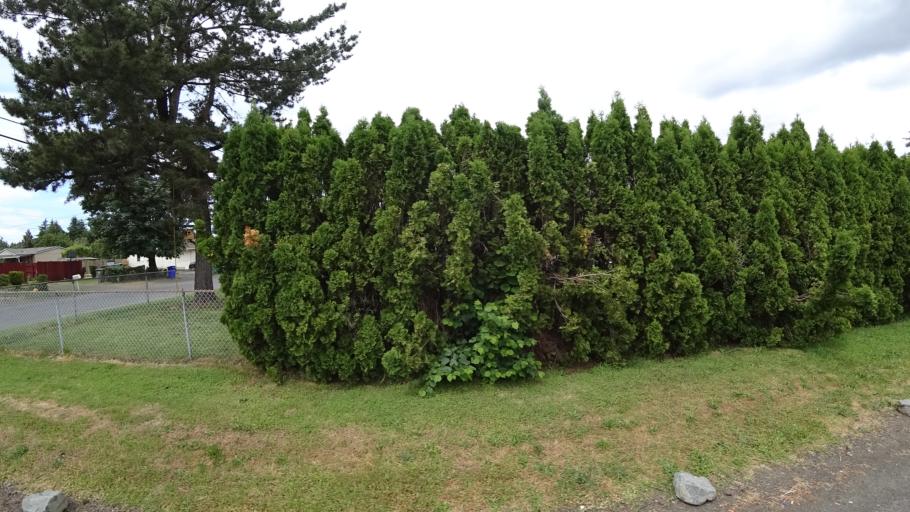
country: US
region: Oregon
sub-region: Multnomah County
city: Lents
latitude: 45.4884
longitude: -122.5418
